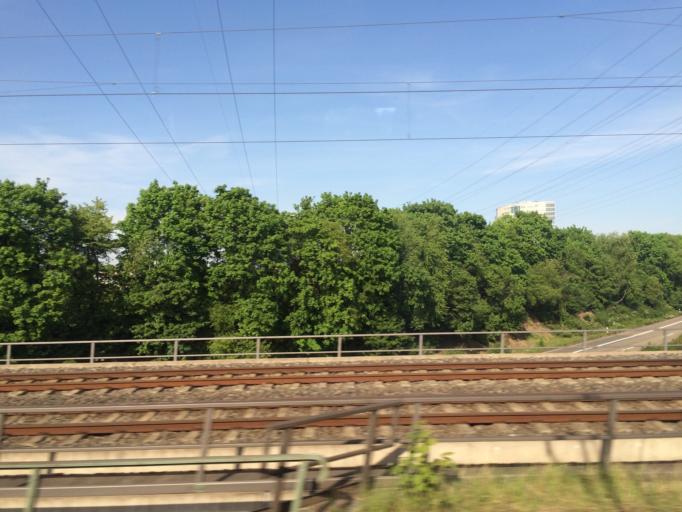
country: DE
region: North Rhine-Westphalia
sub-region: Regierungsbezirk Koln
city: Gremberghoven
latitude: 50.9077
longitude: 7.0477
